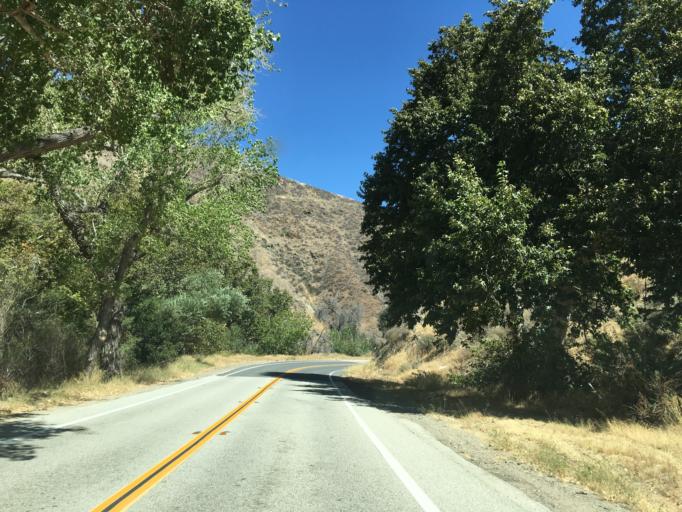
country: US
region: California
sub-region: Los Angeles County
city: Green Valley
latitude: 34.5084
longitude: -118.4528
